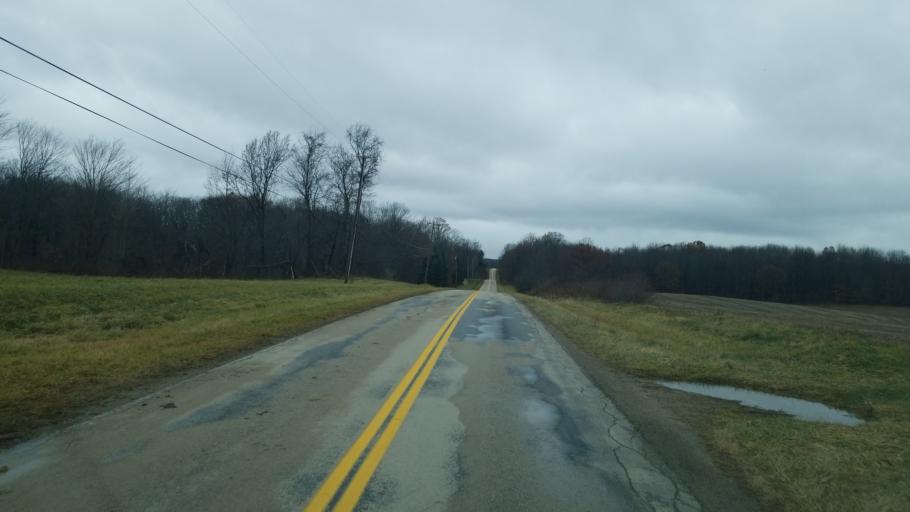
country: US
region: Ohio
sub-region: Ashtabula County
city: North Kingsville
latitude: 41.8633
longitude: -80.6176
